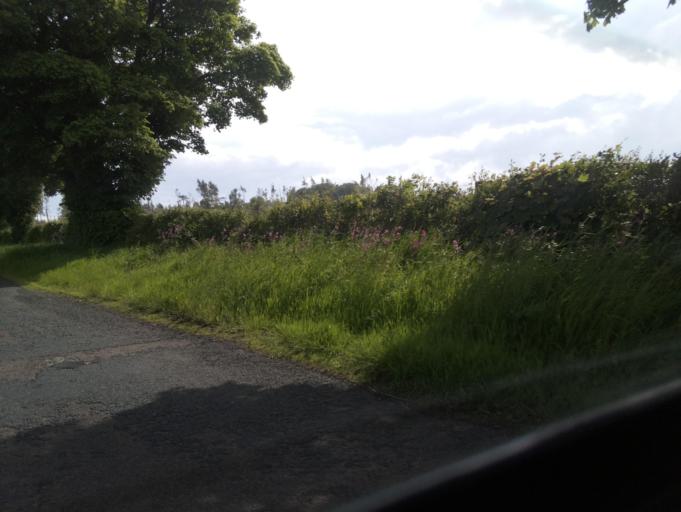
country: GB
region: England
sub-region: Northumberland
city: Alnwick
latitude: 55.4563
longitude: -1.7137
